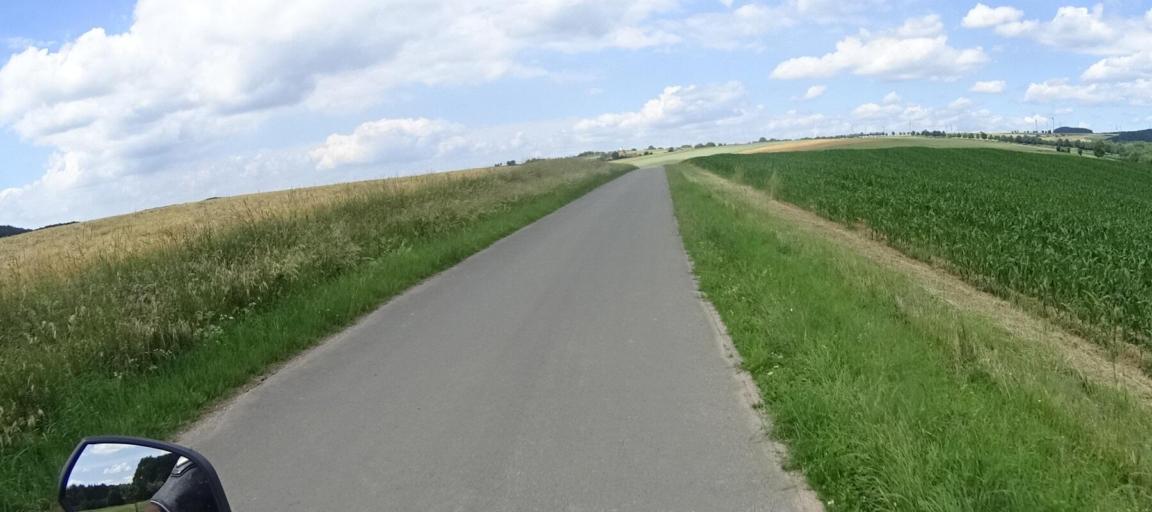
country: DE
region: Lower Saxony
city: Polle
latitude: 51.9122
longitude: 9.3774
